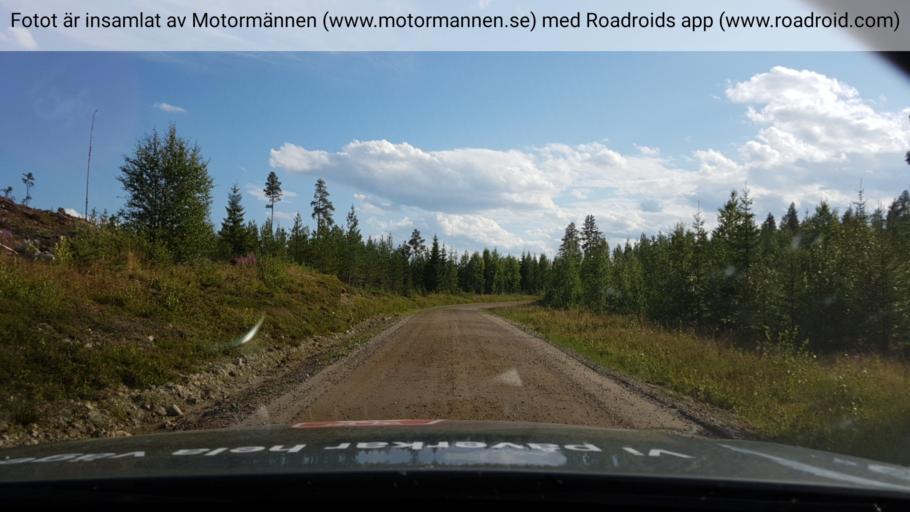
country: SE
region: Jaemtland
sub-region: Stroemsunds Kommun
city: Stroemsund
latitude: 63.7265
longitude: 16.0995
